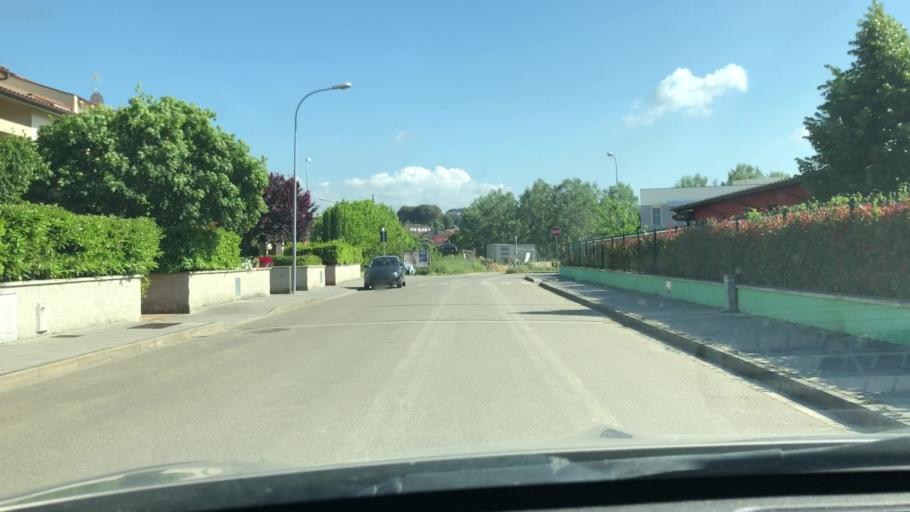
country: IT
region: Tuscany
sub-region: Province of Pisa
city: Capannoli
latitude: 43.5917
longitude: 10.6749
